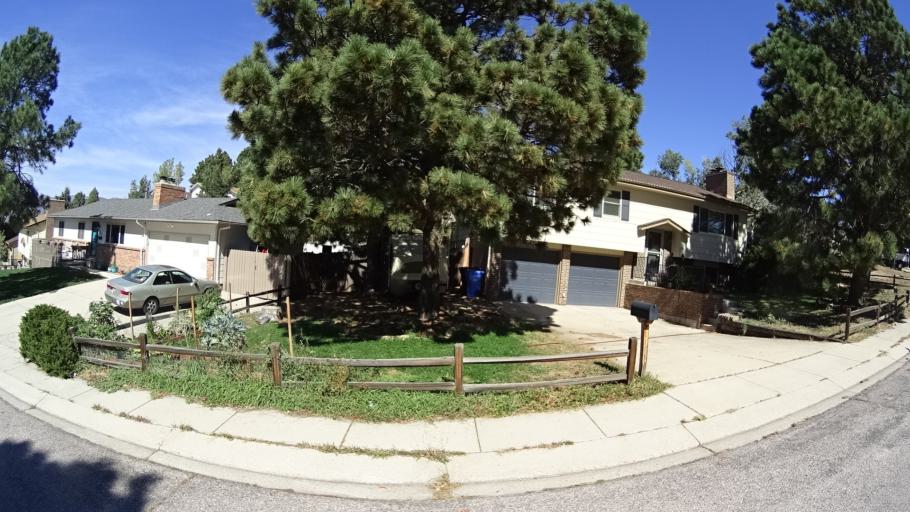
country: US
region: Colorado
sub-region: El Paso County
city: Cimarron Hills
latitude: 38.9119
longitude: -104.7670
